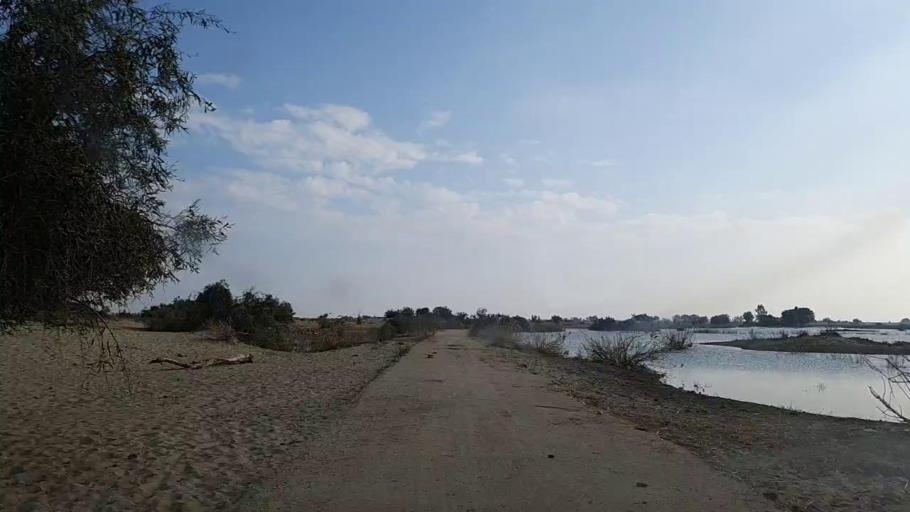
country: PK
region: Sindh
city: Sanghar
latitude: 26.1999
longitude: 69.0298
